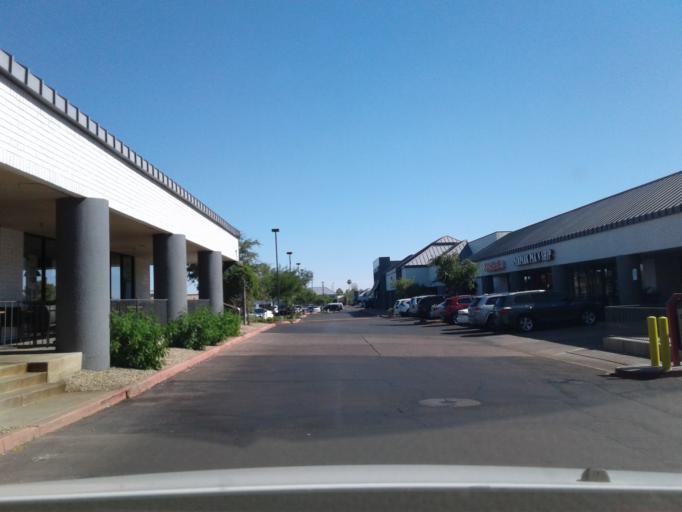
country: US
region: Arizona
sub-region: Maricopa County
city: Paradise Valley
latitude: 33.6148
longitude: -111.9268
